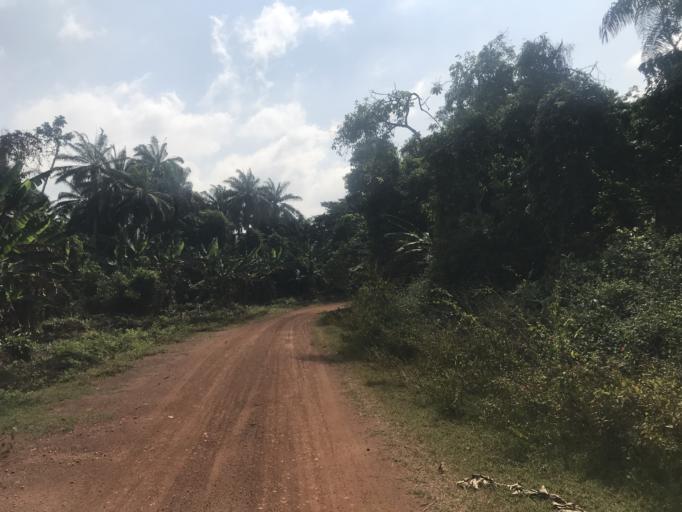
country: NG
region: Osun
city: Ibokun
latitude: 7.8160
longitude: 4.6458
